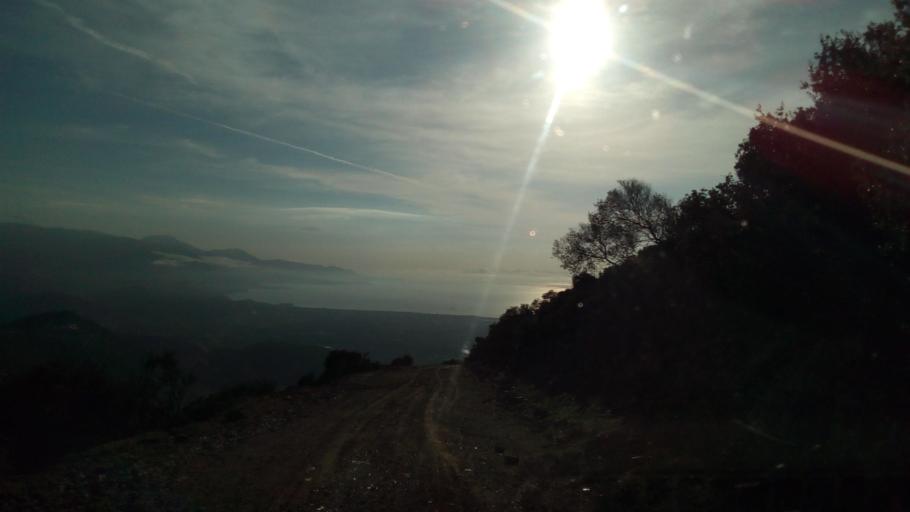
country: GR
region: West Greece
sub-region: Nomos Aitolias kai Akarnanias
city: Nafpaktos
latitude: 38.4140
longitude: 21.8199
